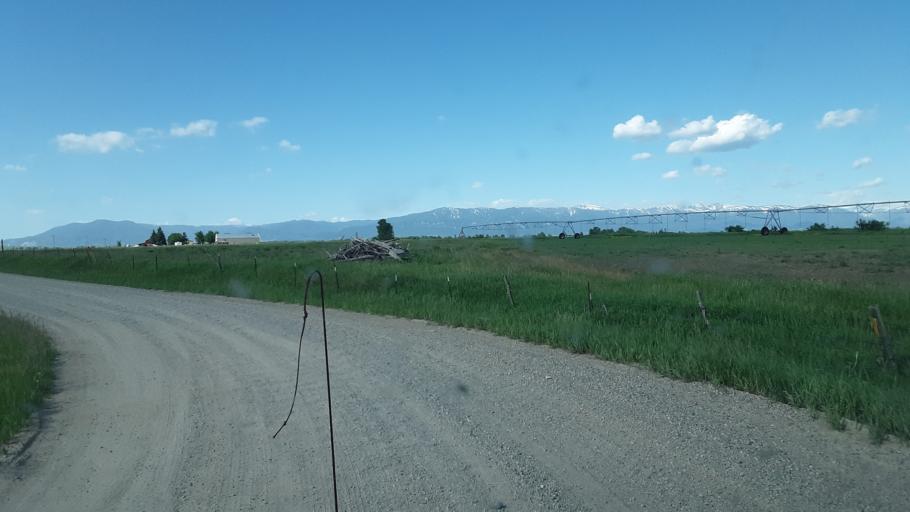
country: US
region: Montana
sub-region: Carbon County
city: Red Lodge
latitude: 45.3404
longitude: -109.1610
